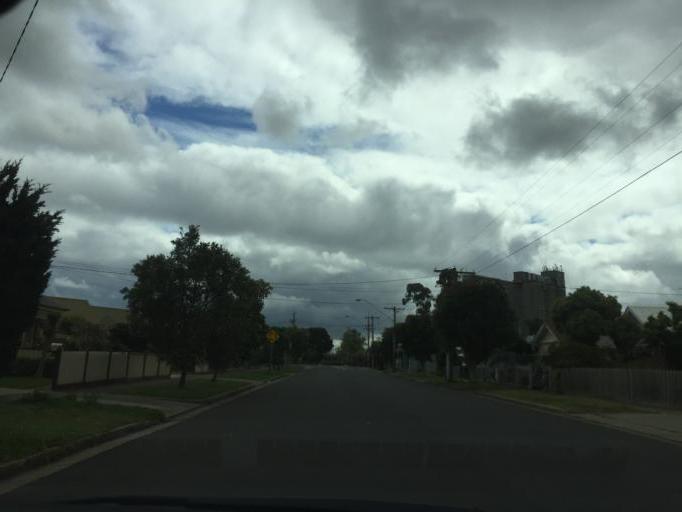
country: AU
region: Victoria
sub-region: Brimbank
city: Sunshine North
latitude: -37.7800
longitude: 144.8228
